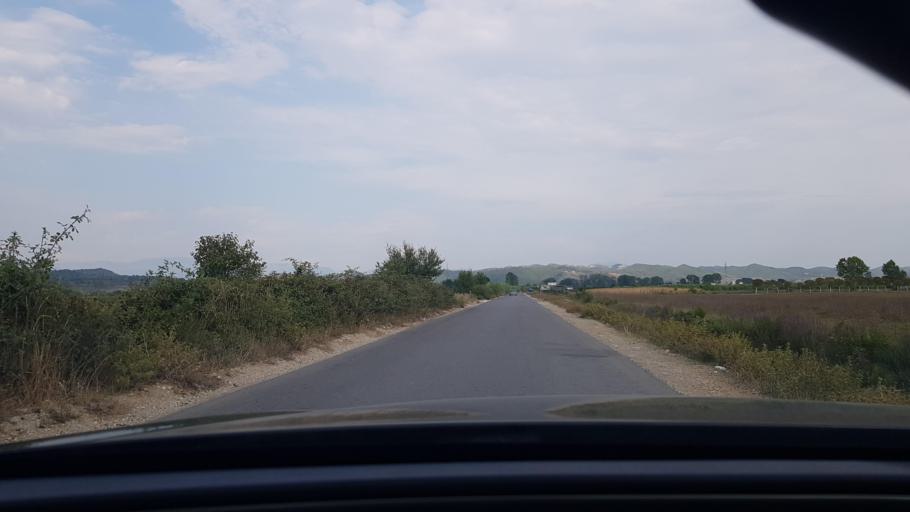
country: AL
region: Durres
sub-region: Rrethi i Durresit
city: Katundi i Ri
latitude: 41.4839
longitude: 19.5320
